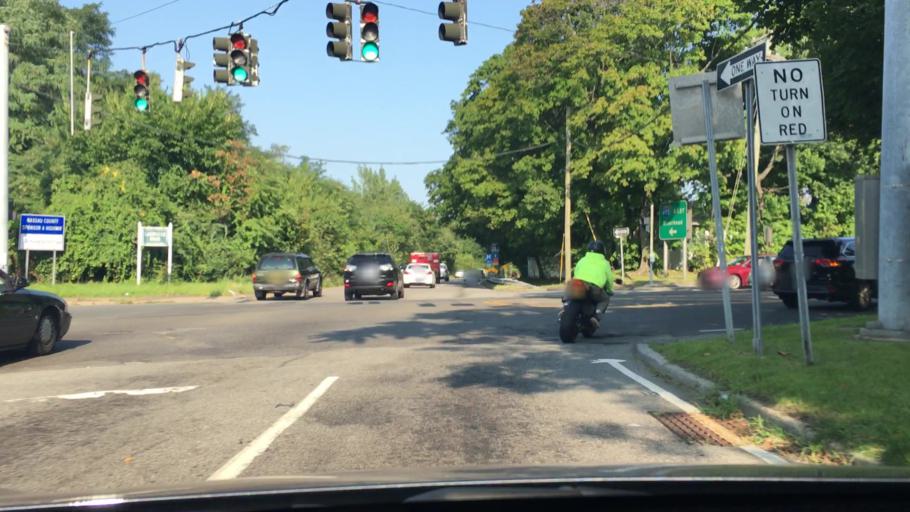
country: US
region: New York
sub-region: Nassau County
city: Lake Success
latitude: 40.7691
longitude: -73.7084
